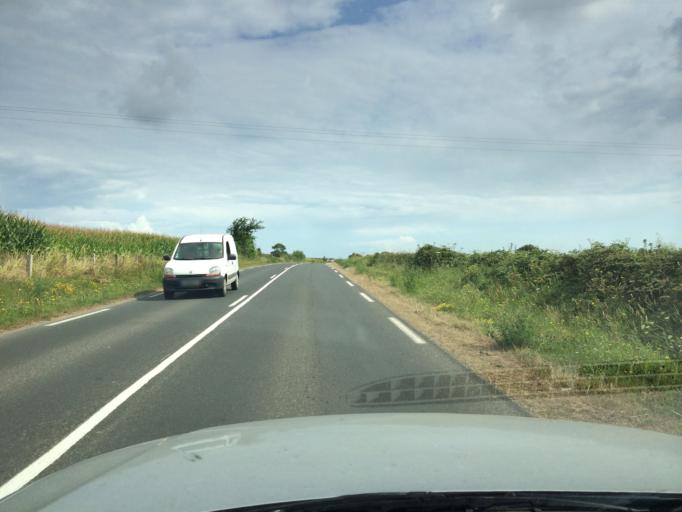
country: FR
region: Lower Normandy
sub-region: Departement de la Manche
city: Saint-Hilaire-Petitville
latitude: 49.3895
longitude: -1.2165
